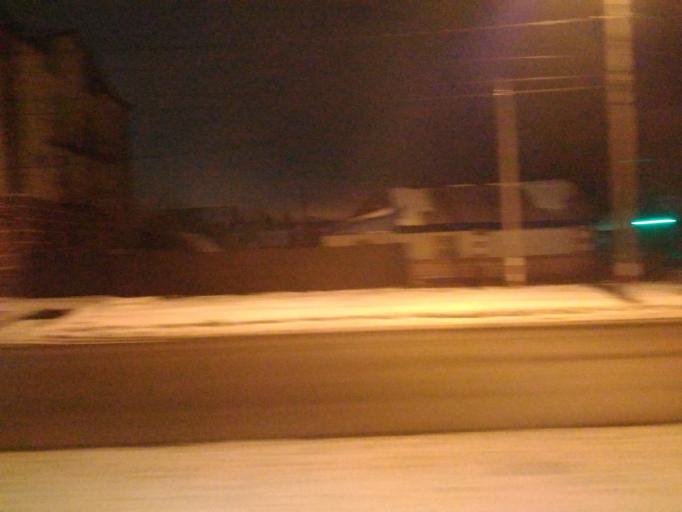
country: RU
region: Ulyanovsk
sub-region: Ulyanovskiy Rayon
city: Ulyanovsk
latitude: 54.3511
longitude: 48.3816
